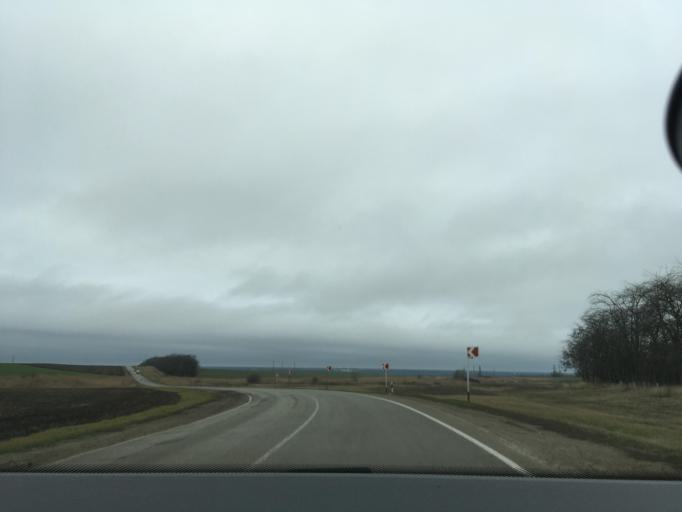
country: RU
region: Krasnodarskiy
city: Kushchevskaya
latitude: 46.5986
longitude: 39.6504
